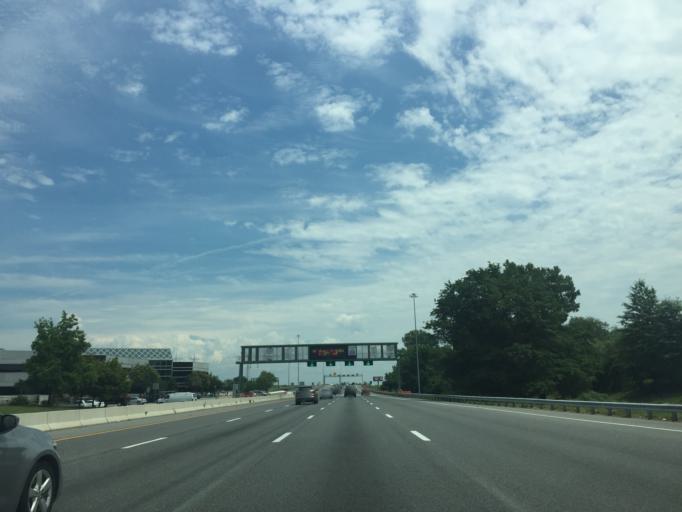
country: US
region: Delaware
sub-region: New Castle County
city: Wilmington Manor
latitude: 39.6954
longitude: -75.5471
